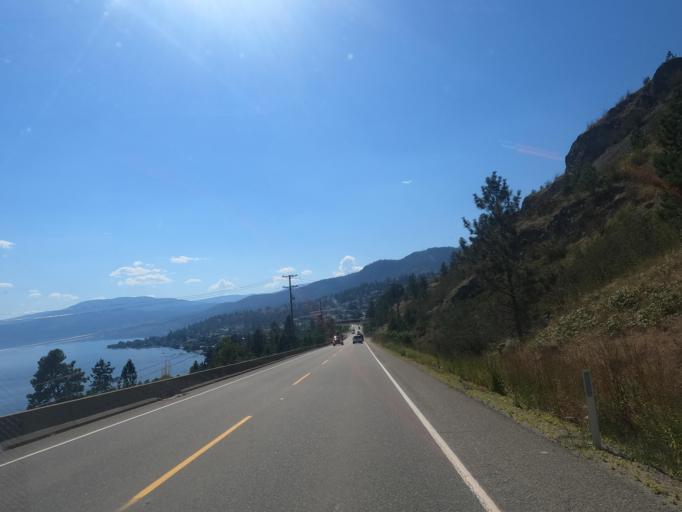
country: CA
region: British Columbia
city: Peachland
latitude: 49.7972
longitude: -119.6897
